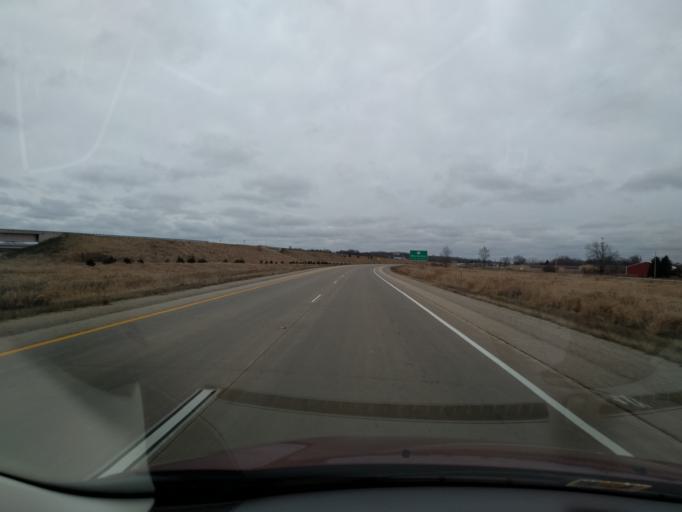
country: US
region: Wisconsin
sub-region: Winnebago County
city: Winneconne
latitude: 44.2086
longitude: -88.6868
